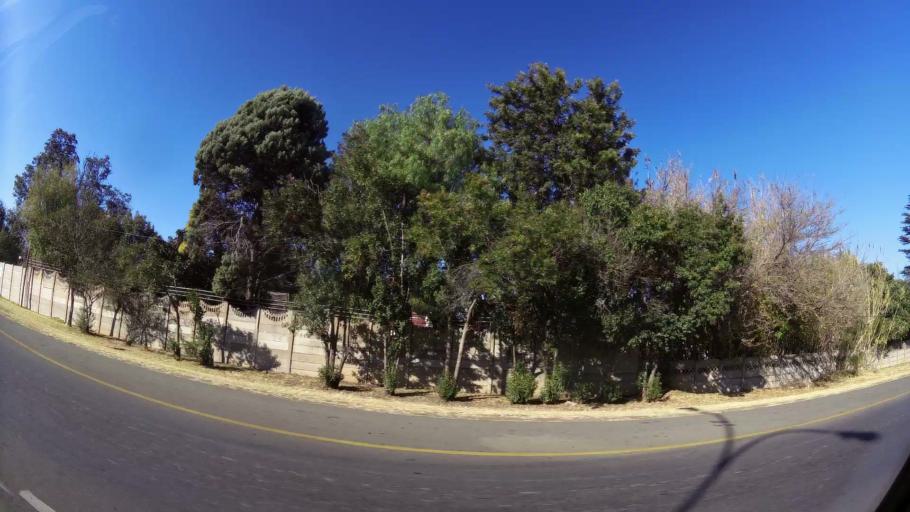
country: ZA
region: Gauteng
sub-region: Ekurhuleni Metropolitan Municipality
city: Germiston
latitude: -26.3117
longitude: 28.0945
